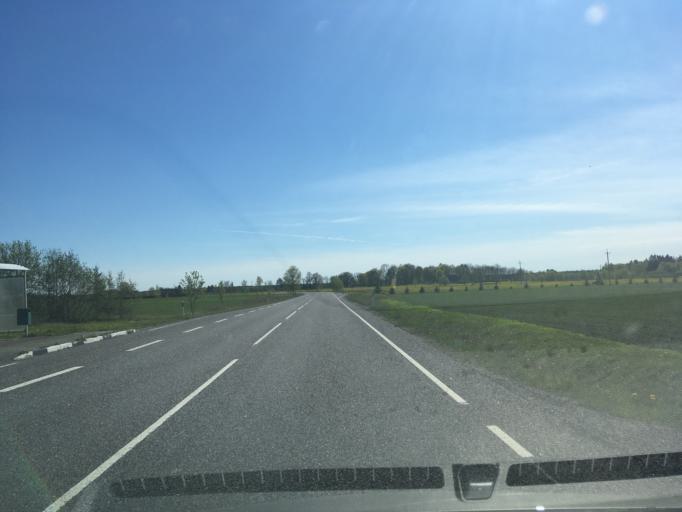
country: EE
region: Harju
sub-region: Rae vald
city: Vaida
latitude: 59.2607
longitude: 25.0203
